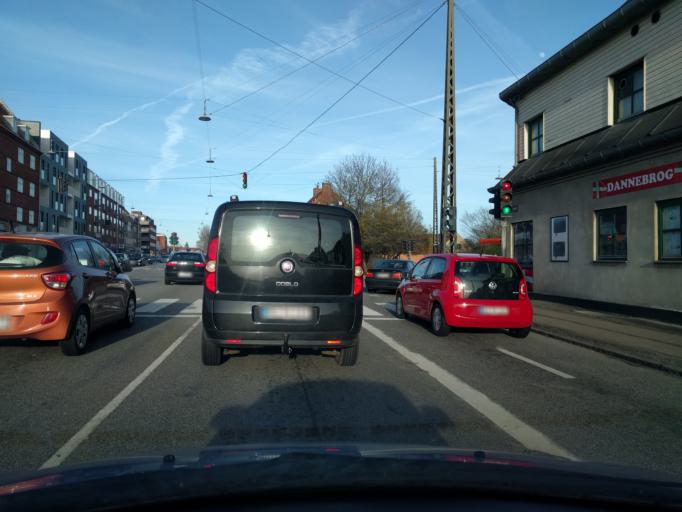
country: DK
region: Capital Region
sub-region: Kobenhavn
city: Vanlose
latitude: 55.6910
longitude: 12.4805
